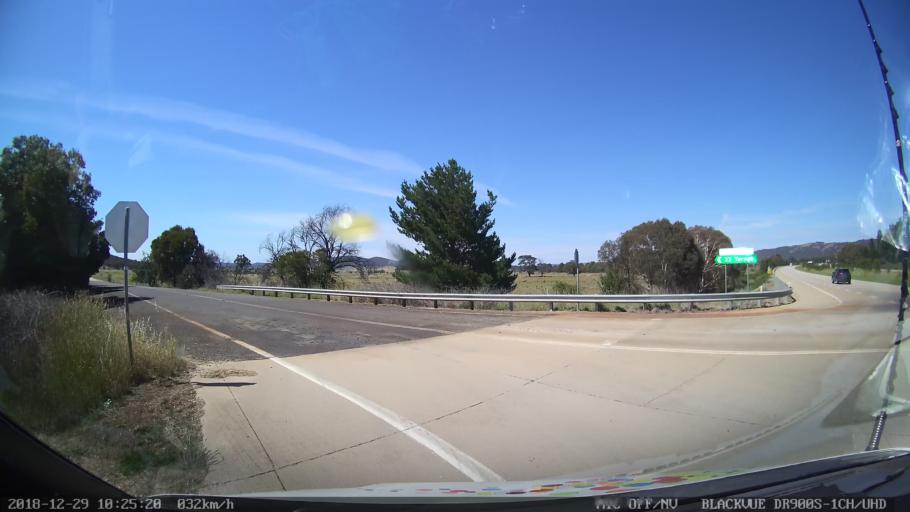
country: AU
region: New South Wales
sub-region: Yass Valley
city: Gundaroo
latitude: -34.9177
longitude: 149.4371
